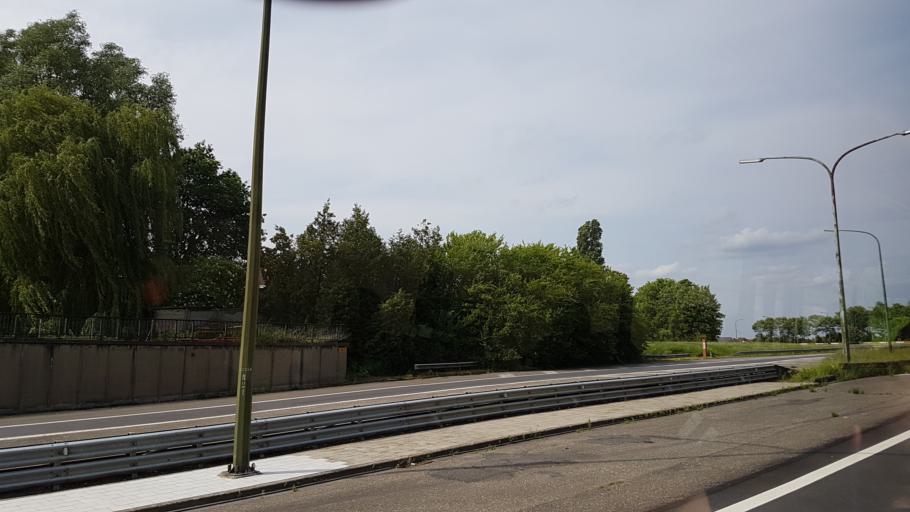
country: BE
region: Flanders
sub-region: Provincie Antwerpen
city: Kapellen
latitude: 51.2890
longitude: 4.4133
